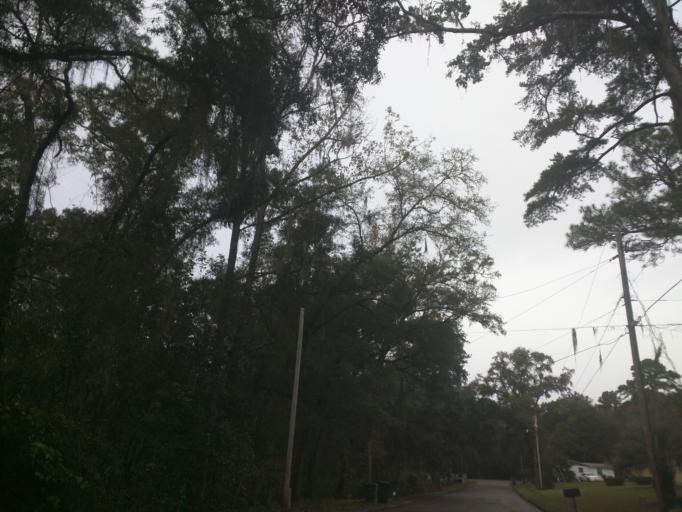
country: US
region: Florida
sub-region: Leon County
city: Tallahassee
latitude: 30.4613
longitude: -84.2346
